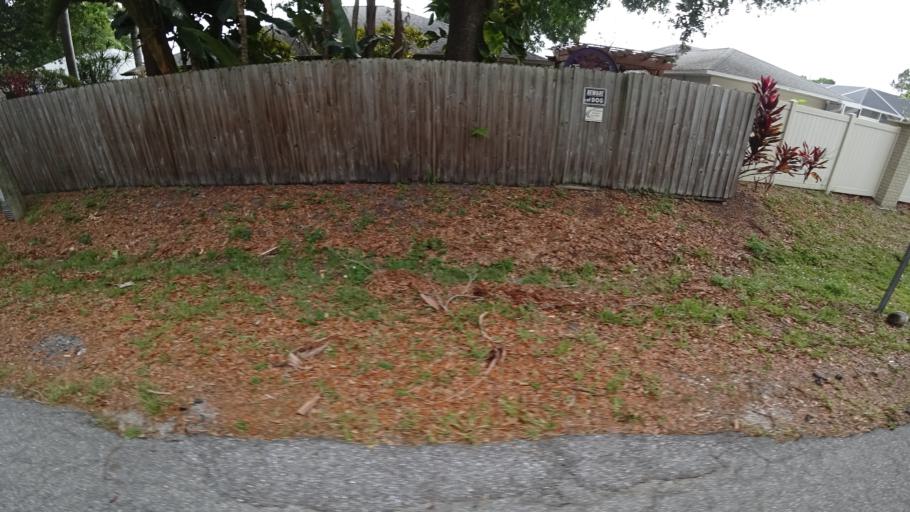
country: US
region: Florida
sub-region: Sarasota County
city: North Sarasota
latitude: 27.4043
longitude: -82.5094
